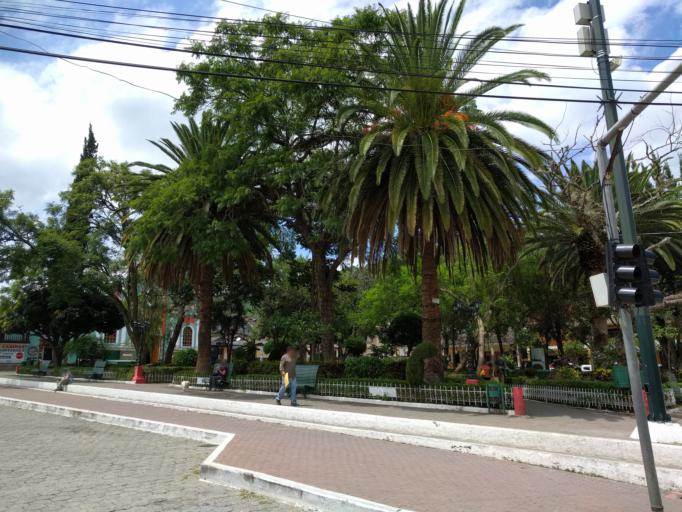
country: EC
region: Loja
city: Loja
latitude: -4.2606
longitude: -79.2223
